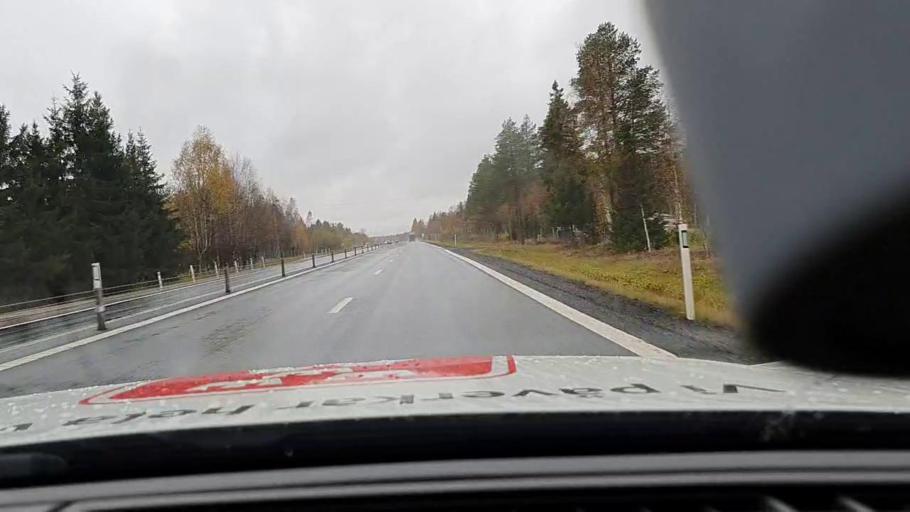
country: SE
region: Norrbotten
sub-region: Haparanda Kommun
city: Haparanda
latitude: 65.8103
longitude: 23.9559
